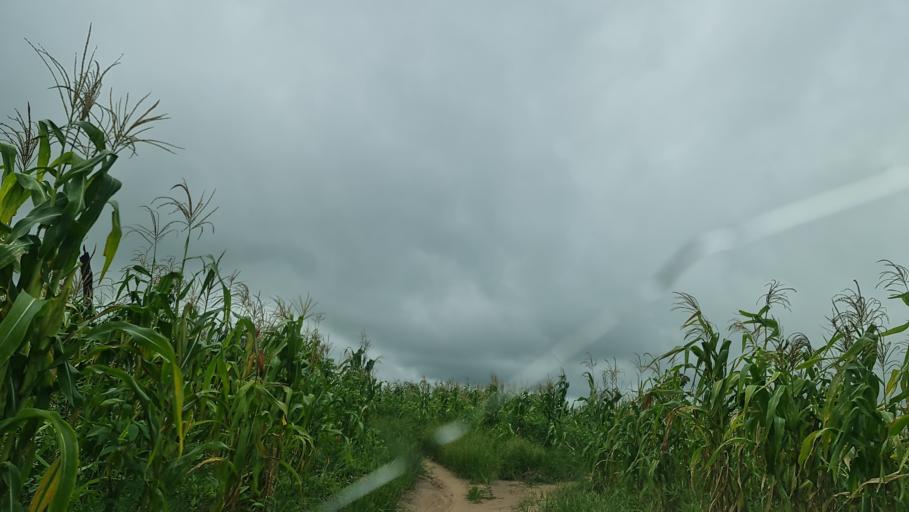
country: MW
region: Southern Region
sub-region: Nsanje District
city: Nsanje
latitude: -17.3436
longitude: 35.7344
